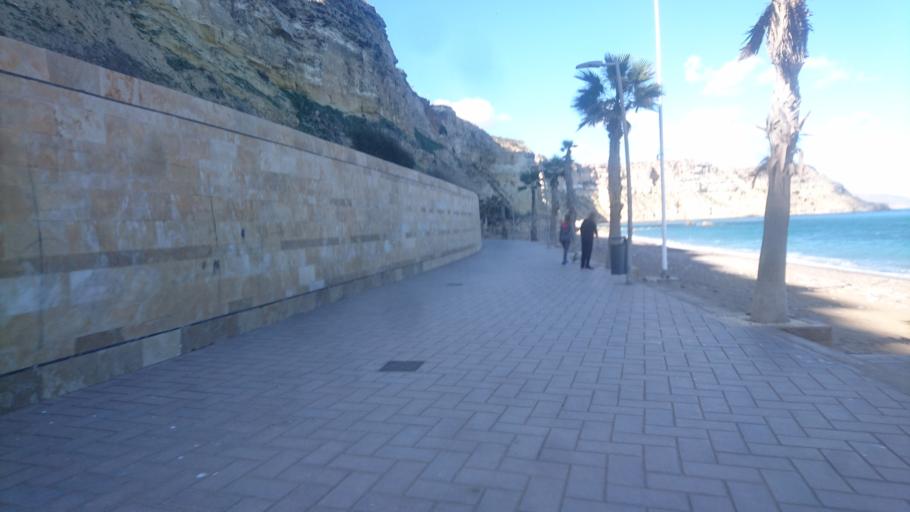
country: ES
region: Melilla
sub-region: Melilla
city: Melilla
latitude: 35.3034
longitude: -2.9426
